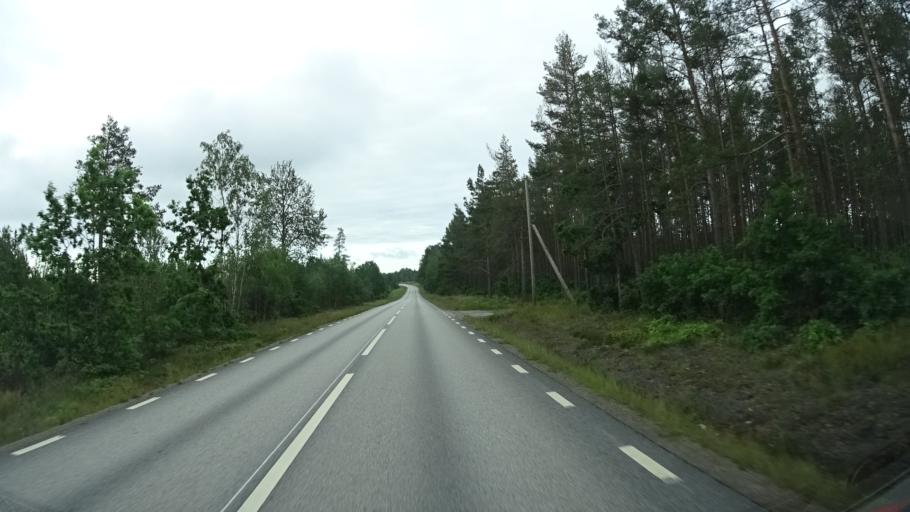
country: SE
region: Kalmar
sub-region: Oskarshamns Kommun
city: Oskarshamn
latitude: 57.2892
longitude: 16.2940
